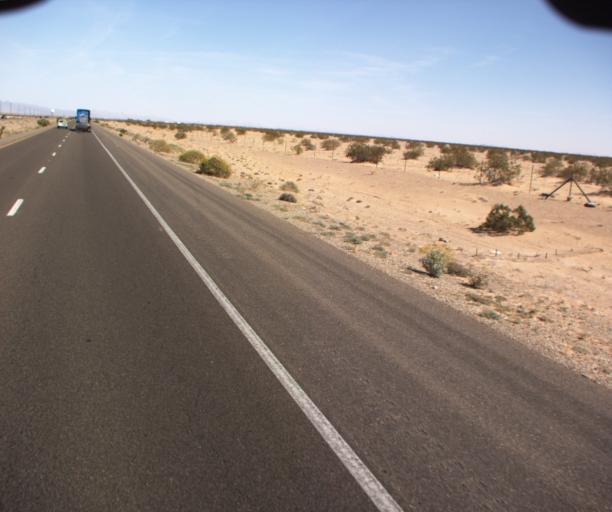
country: MX
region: Sonora
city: San Luis Rio Colorado
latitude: 32.4945
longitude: -114.6808
